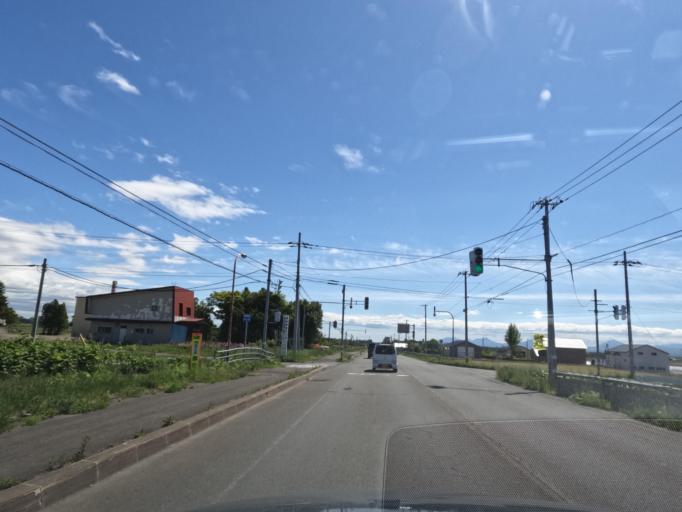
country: JP
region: Hokkaido
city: Kitahiroshima
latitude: 43.0310
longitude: 141.7146
